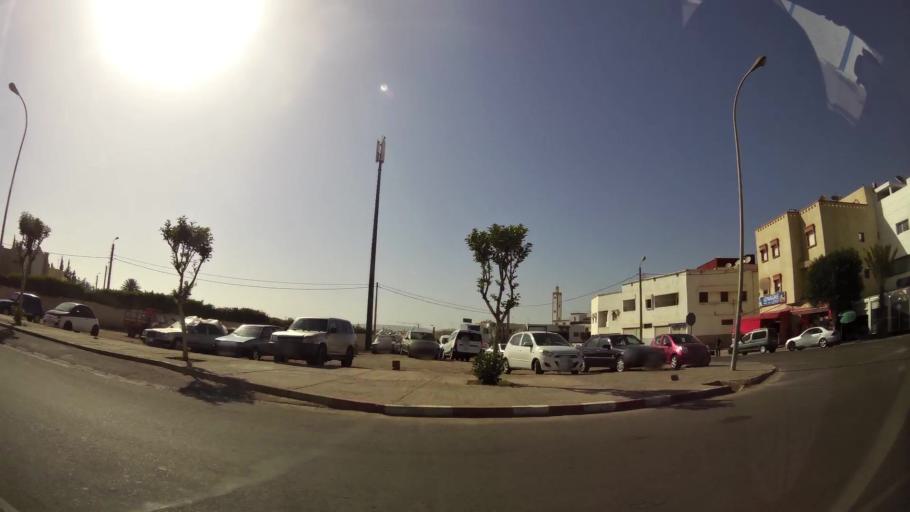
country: MA
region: Oued ed Dahab-Lagouira
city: Dakhla
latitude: 30.4256
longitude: -9.5699
